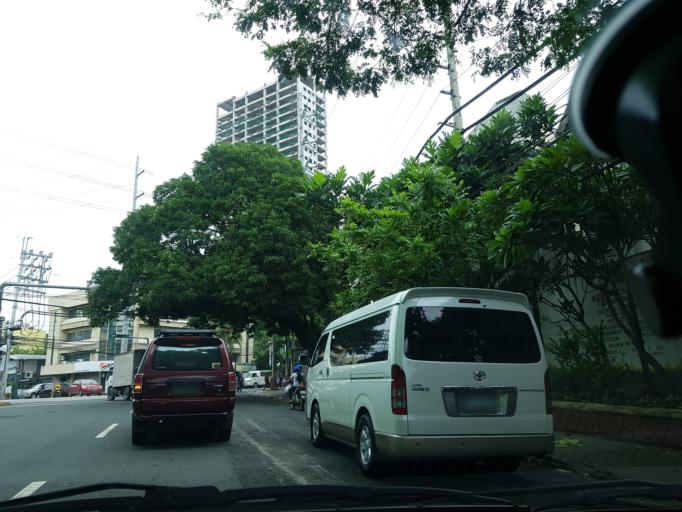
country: PH
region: Metro Manila
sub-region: Pasig
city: Pasig City
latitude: 14.5720
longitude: 121.0650
